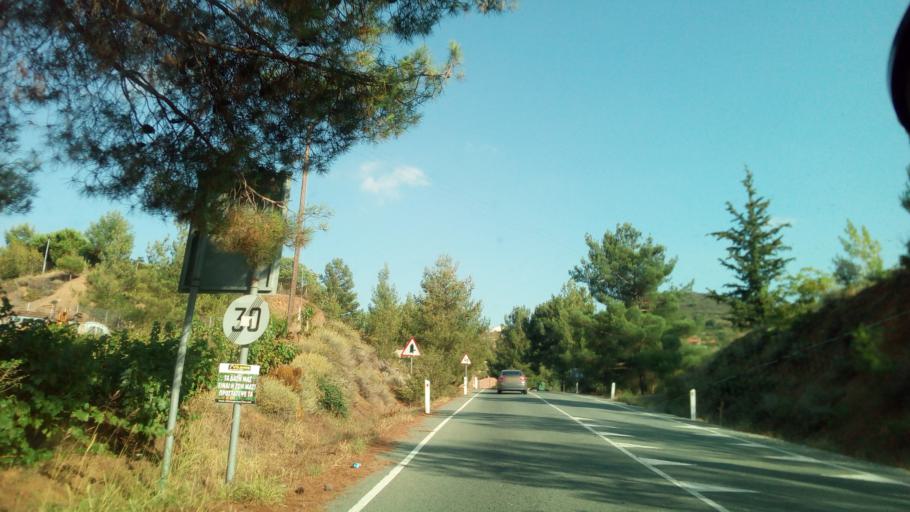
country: CY
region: Limassol
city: Pachna
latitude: 34.8679
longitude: 32.8433
